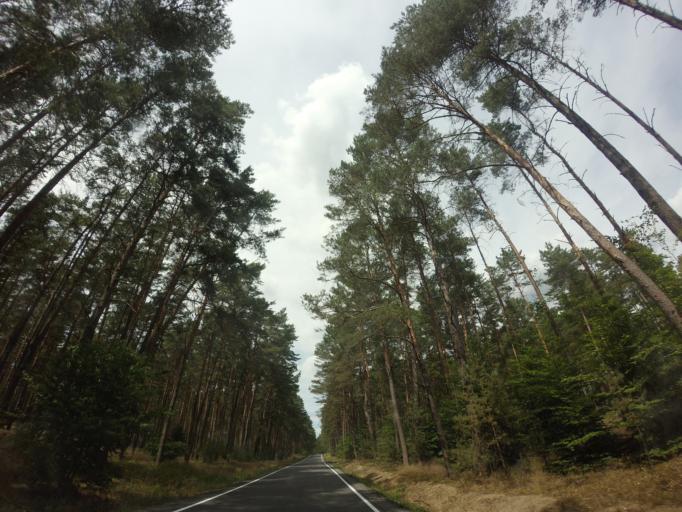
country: PL
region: West Pomeranian Voivodeship
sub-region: Powiat choszczenski
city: Drawno
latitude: 53.1336
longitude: 15.7191
